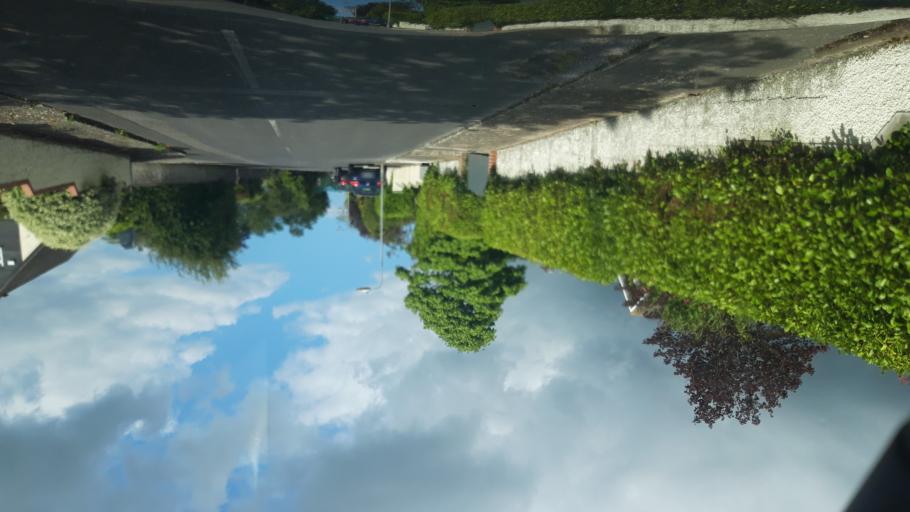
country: IE
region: Munster
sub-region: Waterford
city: Waterford
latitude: 52.2470
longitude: -7.0954
